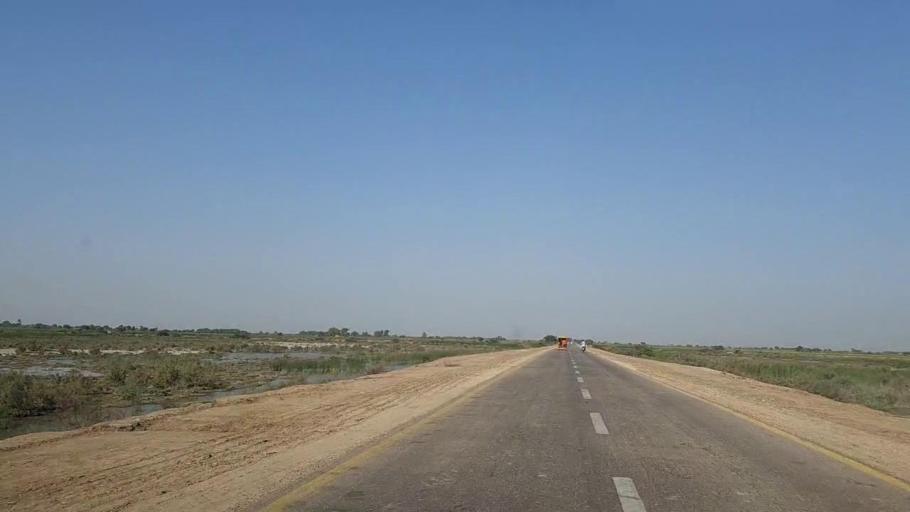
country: PK
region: Sindh
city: Jati
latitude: 24.4046
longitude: 68.2959
